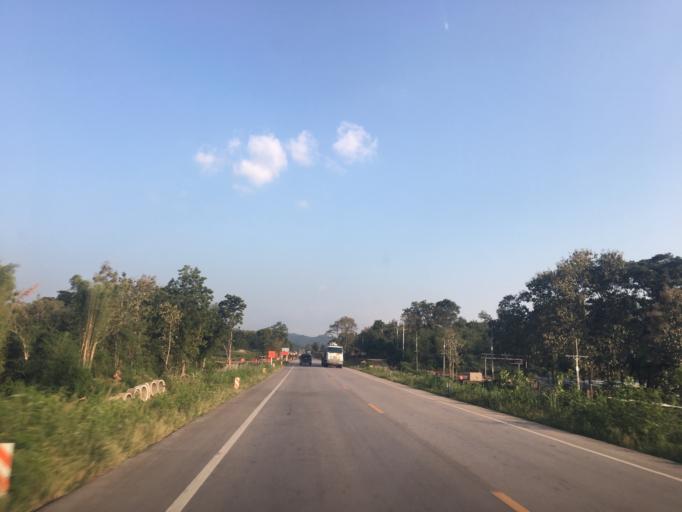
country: TH
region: Lampang
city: Ngao
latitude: 18.7146
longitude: 99.9815
